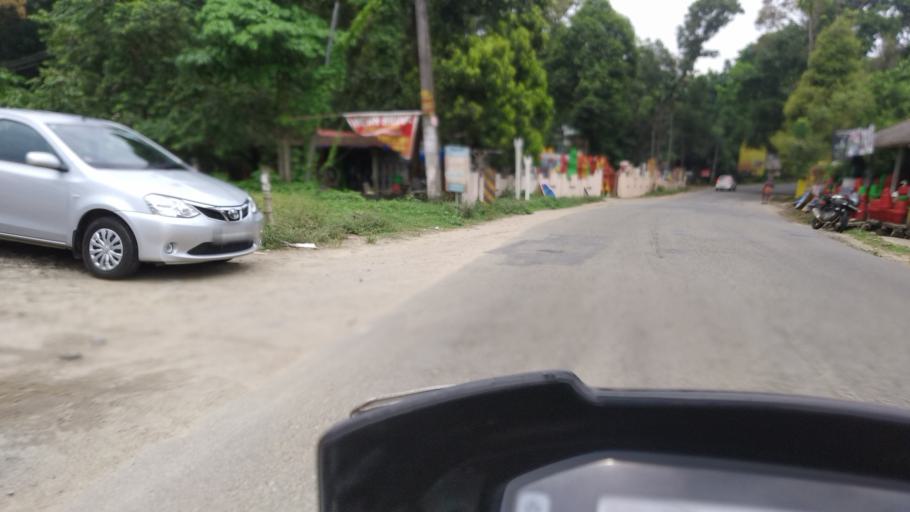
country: IN
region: Kerala
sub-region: Ernakulam
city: Perumpavur
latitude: 10.1087
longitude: 76.5359
